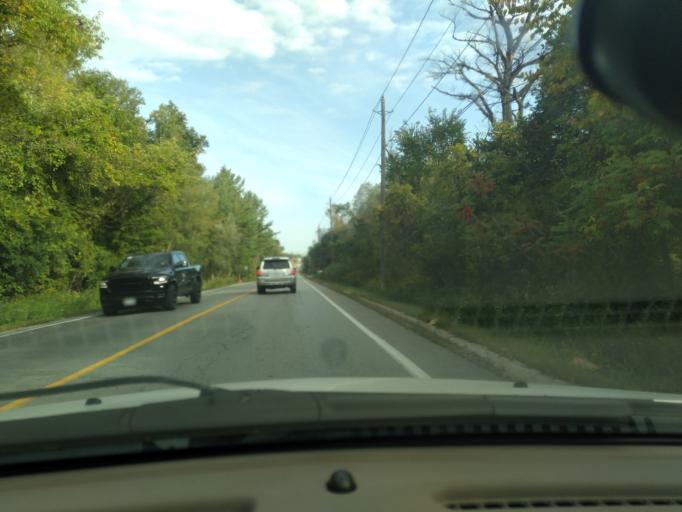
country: CA
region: Ontario
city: Innisfil
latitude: 44.3414
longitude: -79.6625
